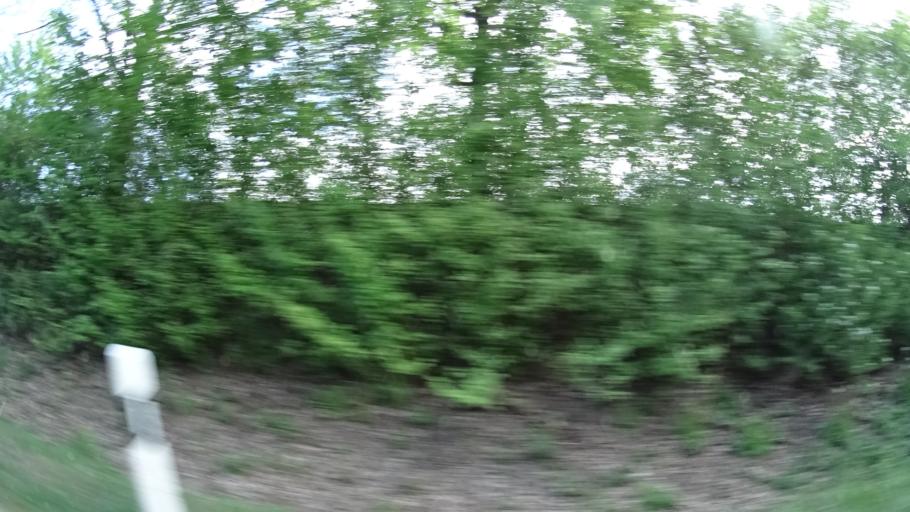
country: DE
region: Baden-Wuerttemberg
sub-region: Tuebingen Region
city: Haigerloch
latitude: 48.3628
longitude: 8.7813
